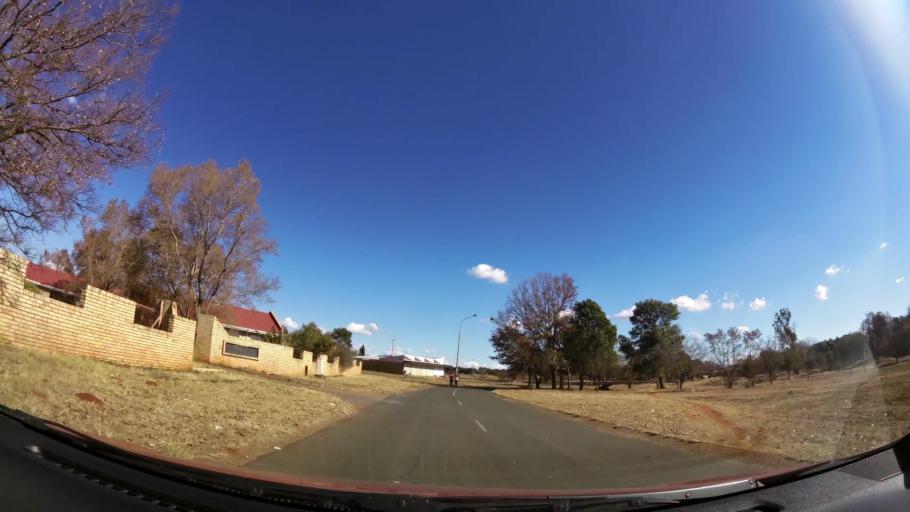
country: ZA
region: Gauteng
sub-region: West Rand District Municipality
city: Carletonville
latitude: -26.3676
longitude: 27.3853
